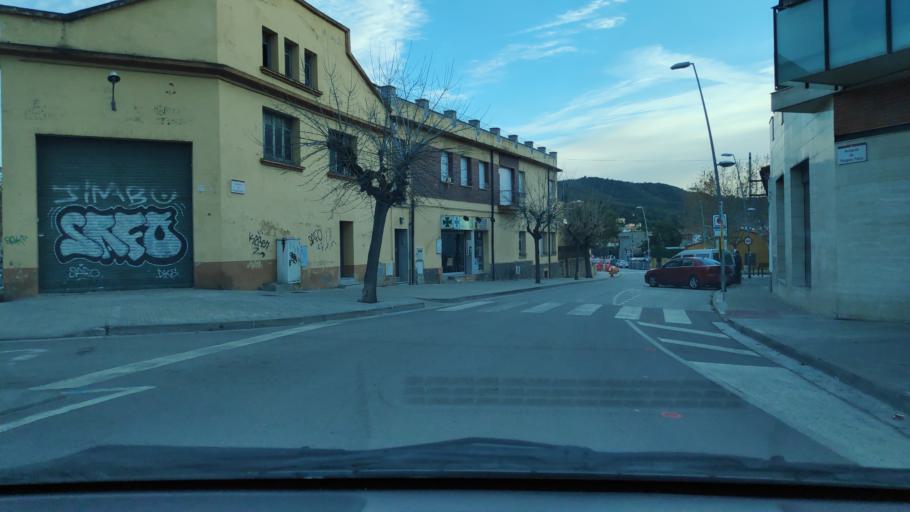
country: ES
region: Catalonia
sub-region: Provincia de Barcelona
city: Montmelo
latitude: 41.5506
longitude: 2.2488
